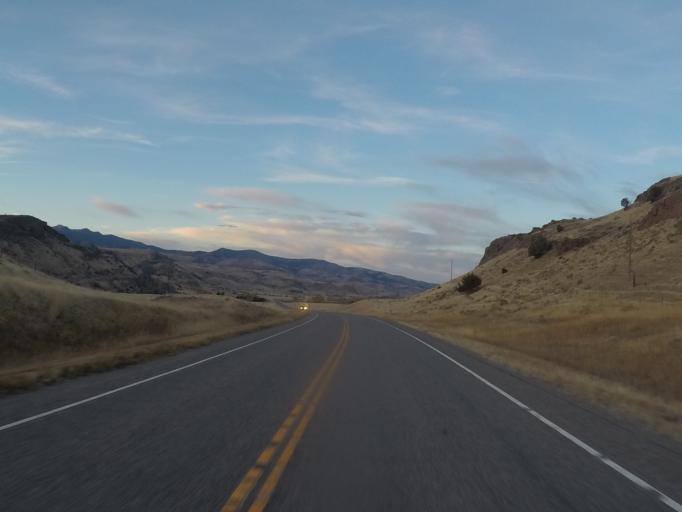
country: US
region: Montana
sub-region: Gallatin County
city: Bozeman
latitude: 45.2403
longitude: -110.8703
